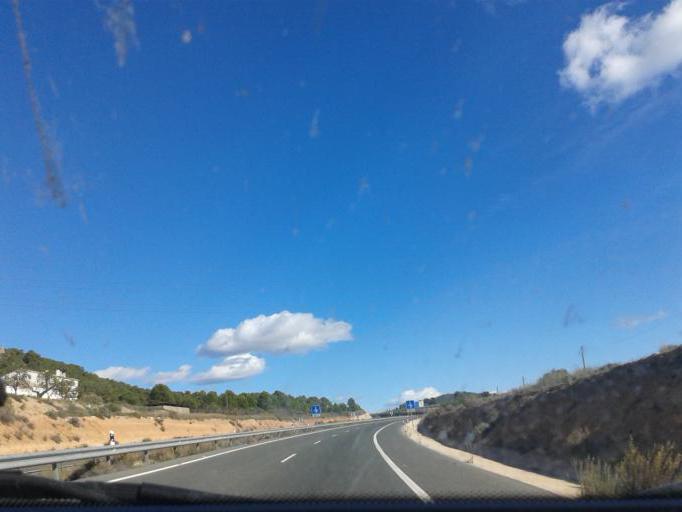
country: ES
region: Valencia
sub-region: Provincia de Alicante
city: Biar
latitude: 38.5932
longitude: -0.7432
